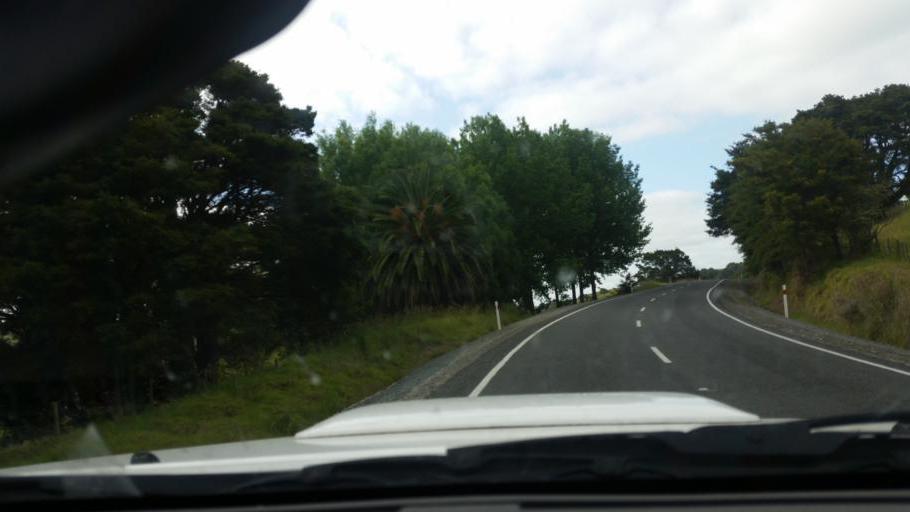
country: NZ
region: Northland
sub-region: Kaipara District
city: Dargaville
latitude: -35.8439
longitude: 173.8441
